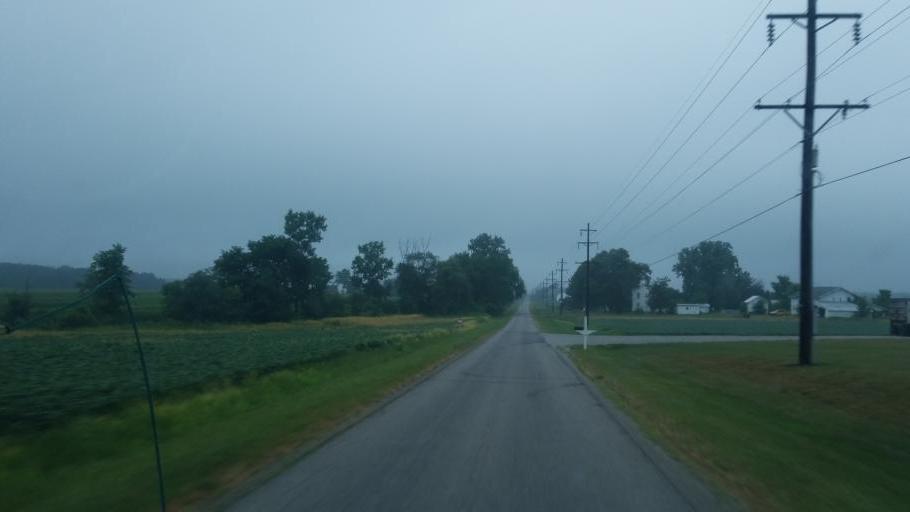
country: US
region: Ohio
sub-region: Defiance County
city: Hicksville
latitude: 41.3538
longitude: -84.7239
